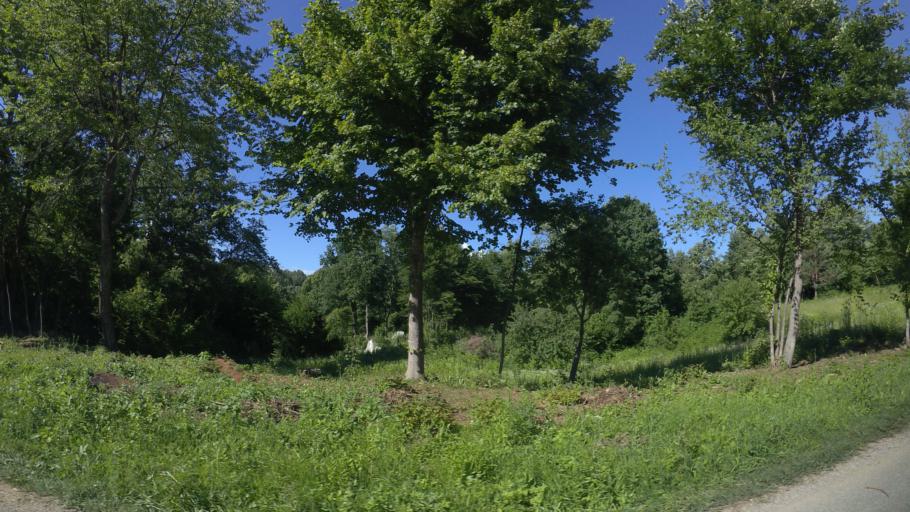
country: HR
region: Karlovacka
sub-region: Grad Karlovac
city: Slunj
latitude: 45.1471
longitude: 15.5709
